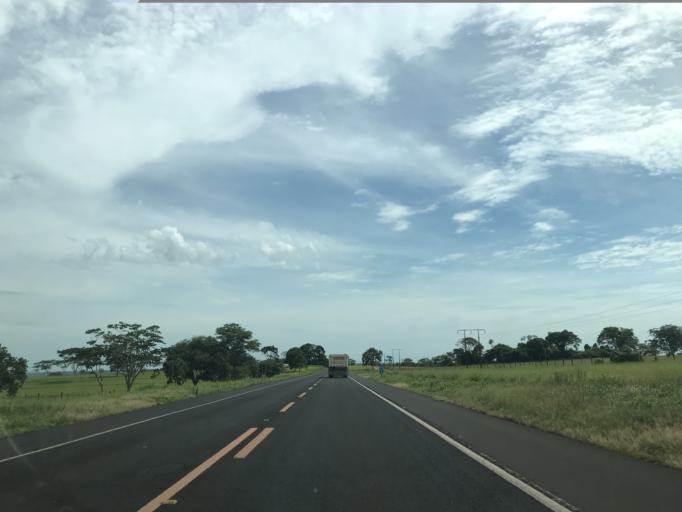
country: BR
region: Sao Paulo
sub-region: Nova Granada
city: Nova Granada
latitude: -20.3747
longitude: -49.2277
